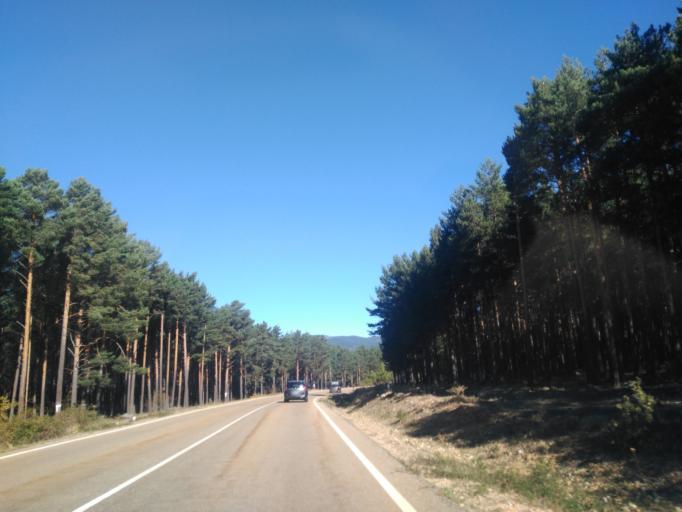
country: ES
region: Castille and Leon
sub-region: Provincia de Soria
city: Vinuesa
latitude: 41.9560
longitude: -2.7766
